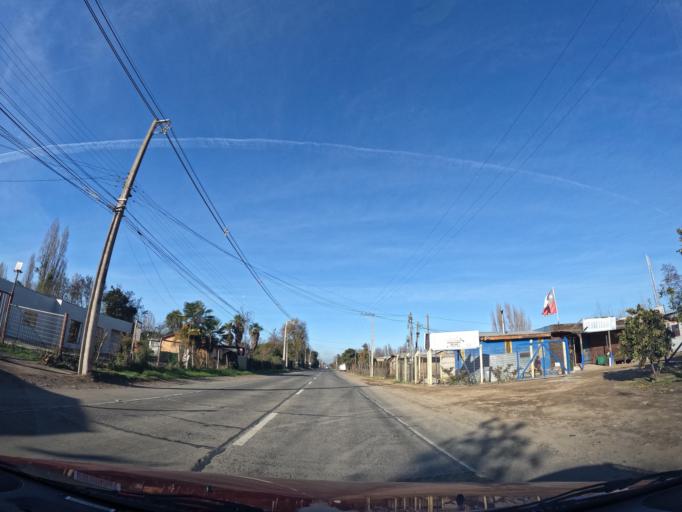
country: CL
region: Maule
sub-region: Provincia de Linares
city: San Javier
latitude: -35.5748
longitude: -71.6701
